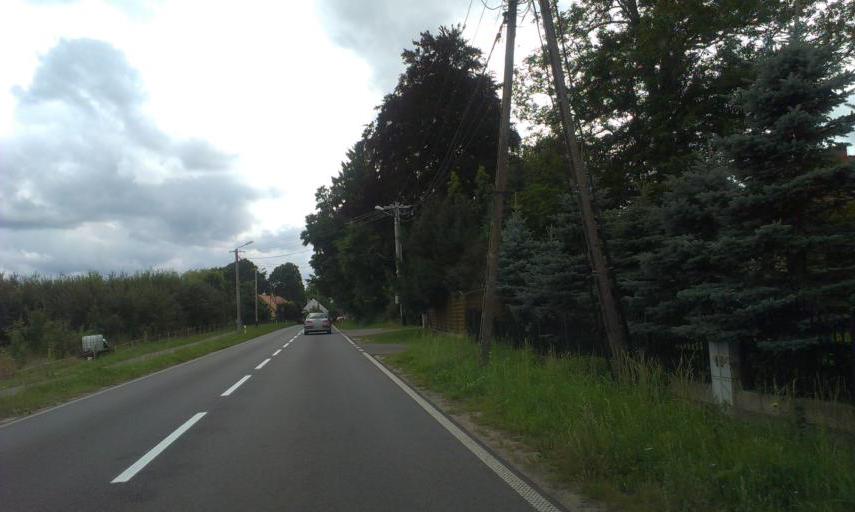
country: PL
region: West Pomeranian Voivodeship
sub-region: Koszalin
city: Koszalin
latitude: 54.1252
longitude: 16.1687
